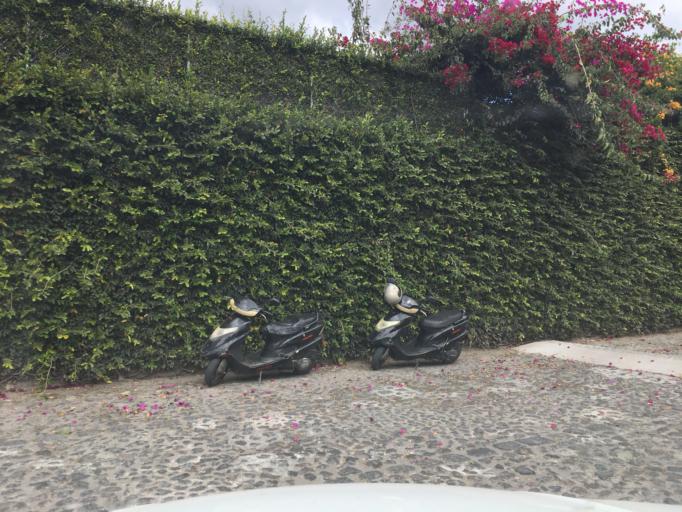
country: GT
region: Sacatepequez
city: Antigua Guatemala
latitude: 14.5497
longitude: -90.7382
